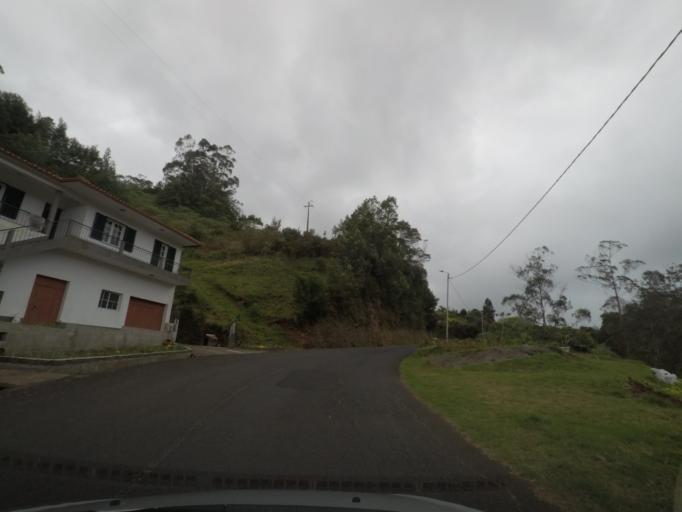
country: PT
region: Madeira
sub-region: Santa Cruz
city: Santa Cruz
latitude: 32.7437
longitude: -16.8250
